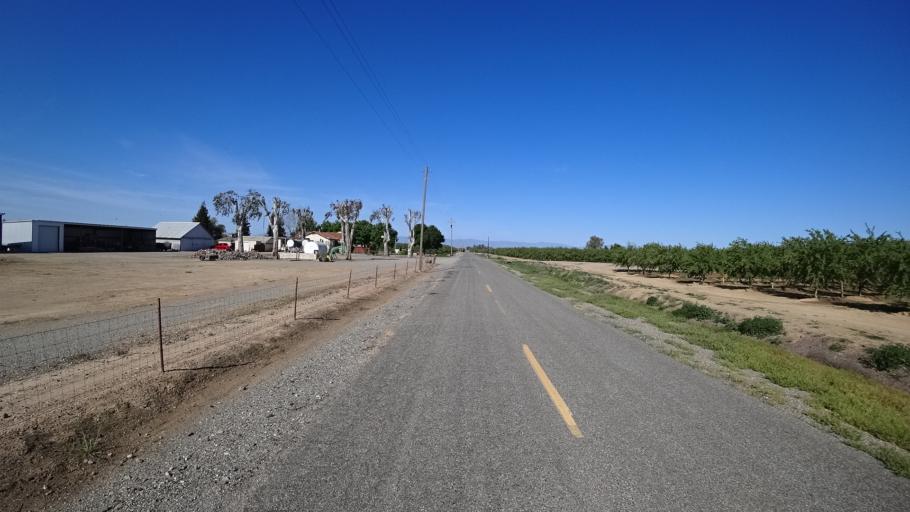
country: US
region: California
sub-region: Glenn County
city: Willows
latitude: 39.6113
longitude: -122.1693
